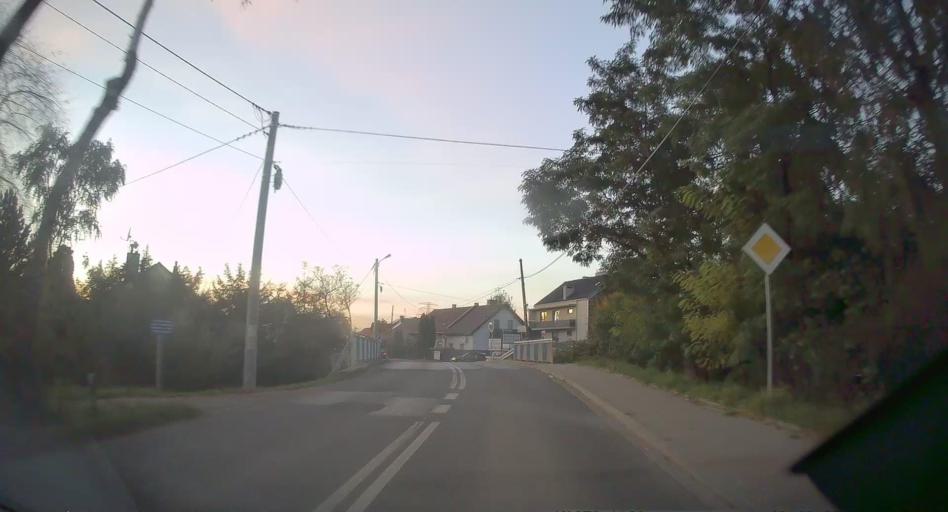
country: PL
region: Lesser Poland Voivodeship
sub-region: Powiat krakowski
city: Zabierzow
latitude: 50.1214
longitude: 19.8232
